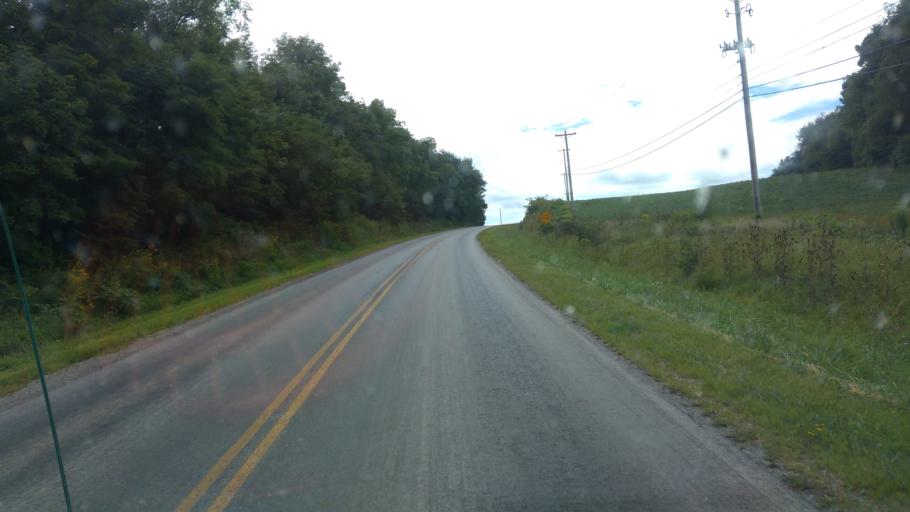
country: US
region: Ohio
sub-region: Holmes County
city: Millersburg
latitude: 40.5544
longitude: -81.7982
